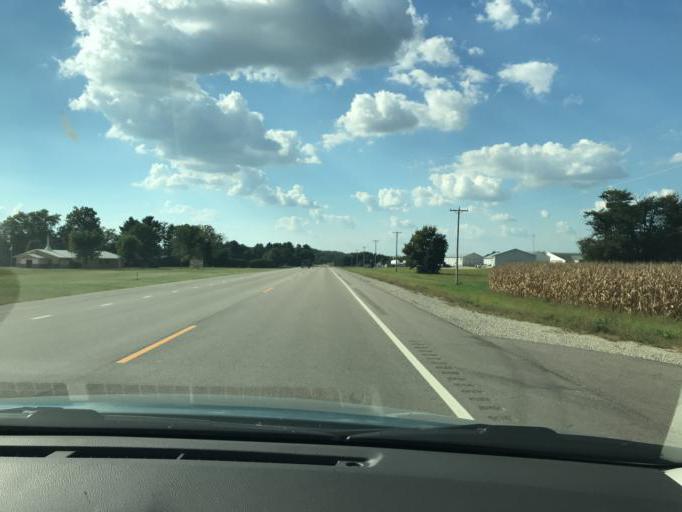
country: US
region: Wisconsin
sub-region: Green County
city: Brodhead
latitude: 42.5875
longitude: -89.3904
